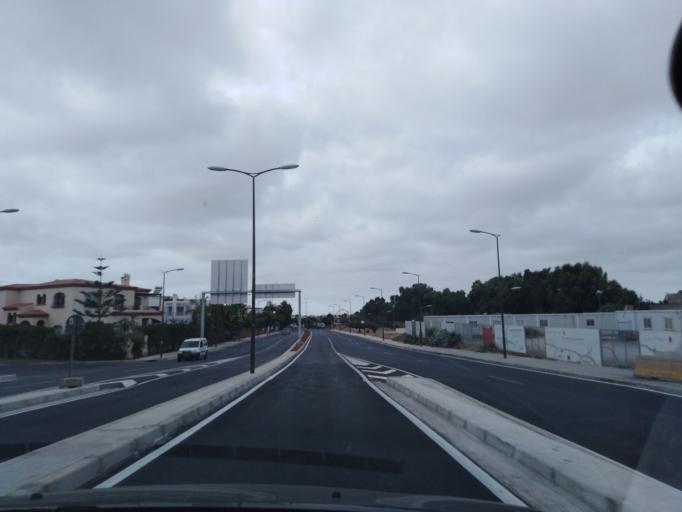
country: MA
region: Grand Casablanca
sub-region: Casablanca
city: Casablanca
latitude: 33.5401
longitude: -7.6631
